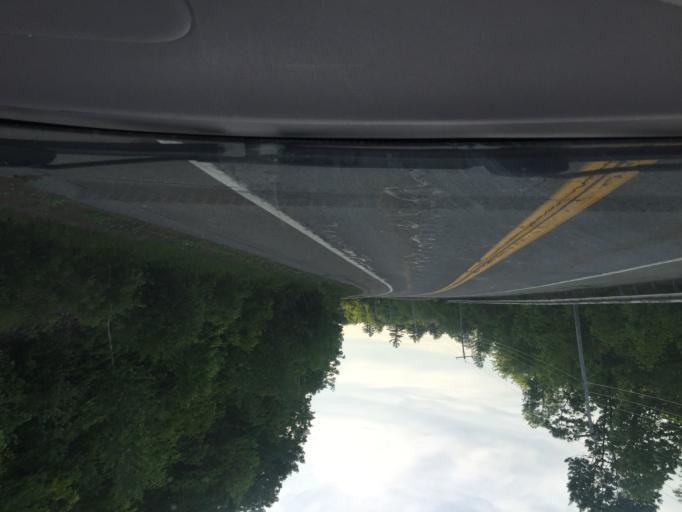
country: US
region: Massachusetts
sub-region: Middlesex County
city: Ashby
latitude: 42.6870
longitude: -71.8565
